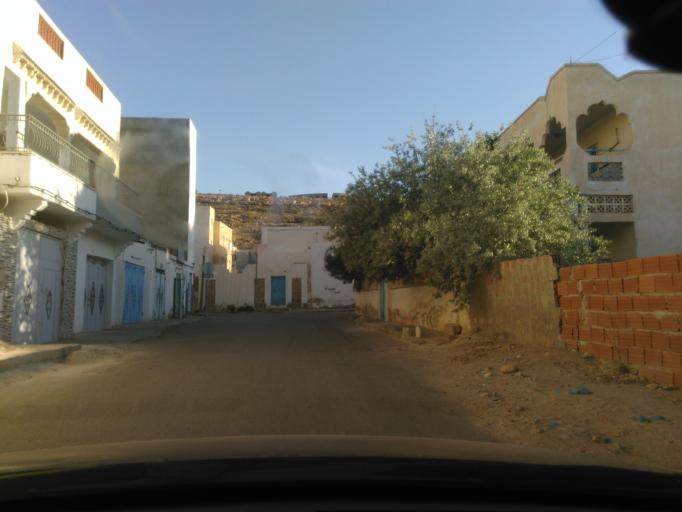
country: TN
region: Tataouine
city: Tataouine
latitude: 32.9270
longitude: 10.4518
